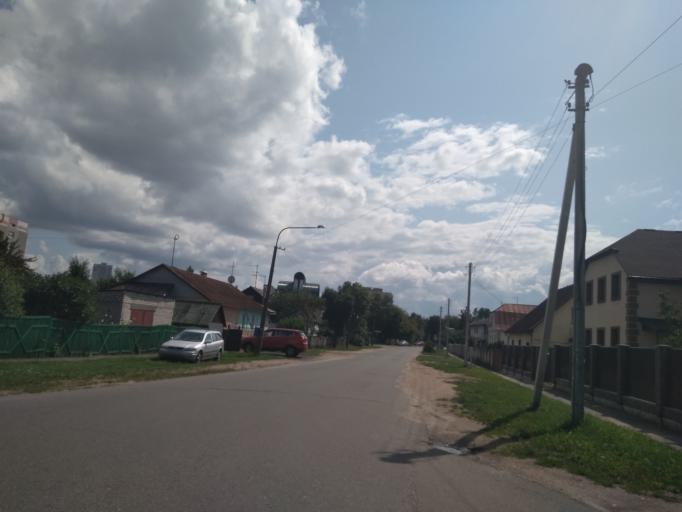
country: BY
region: Minsk
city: Minsk
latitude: 53.9362
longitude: 27.5554
